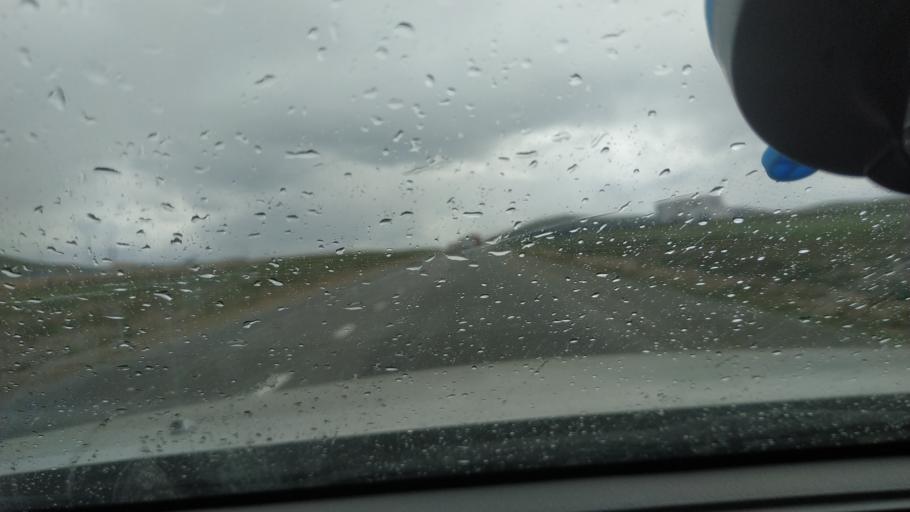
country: MN
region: Ulaanbaatar
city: Ulaanbaatar
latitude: 47.8059
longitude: 106.7496
